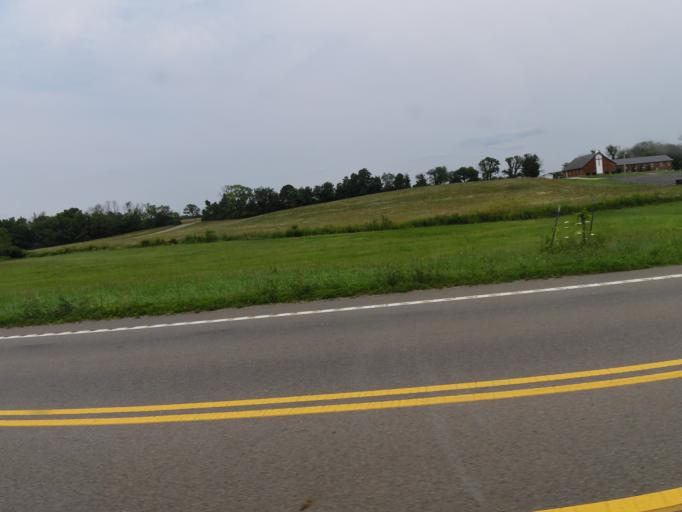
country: US
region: Ohio
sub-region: Warren County
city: Waynesville
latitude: 39.4986
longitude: -83.9922
